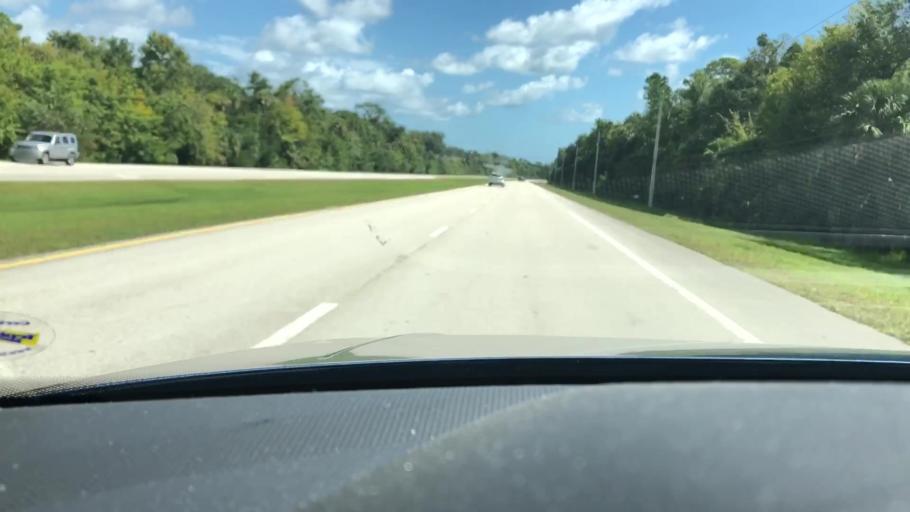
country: US
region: Florida
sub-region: Volusia County
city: Edgewater
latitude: 28.9584
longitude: -80.9294
